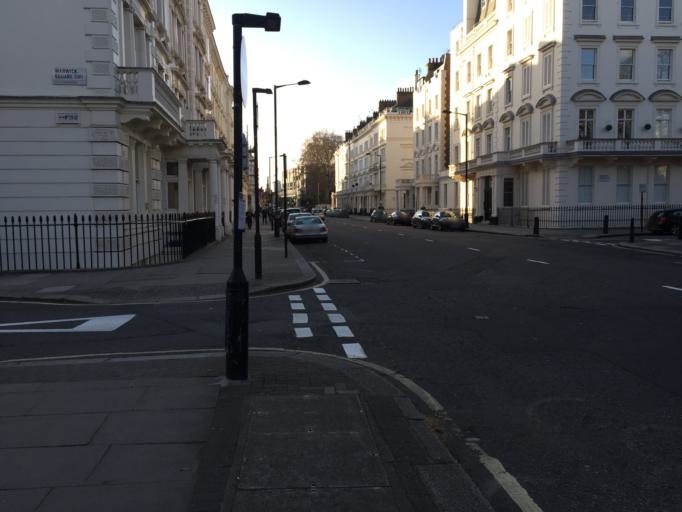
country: GB
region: England
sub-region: Greater London
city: Battersea
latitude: 51.4900
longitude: -0.1421
